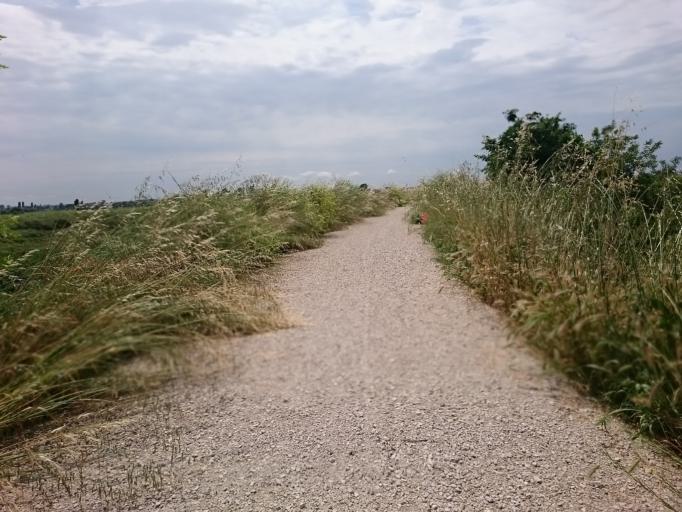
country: IT
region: Veneto
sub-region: Provincia di Padova
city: Carceri
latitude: 45.1899
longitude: 11.6411
